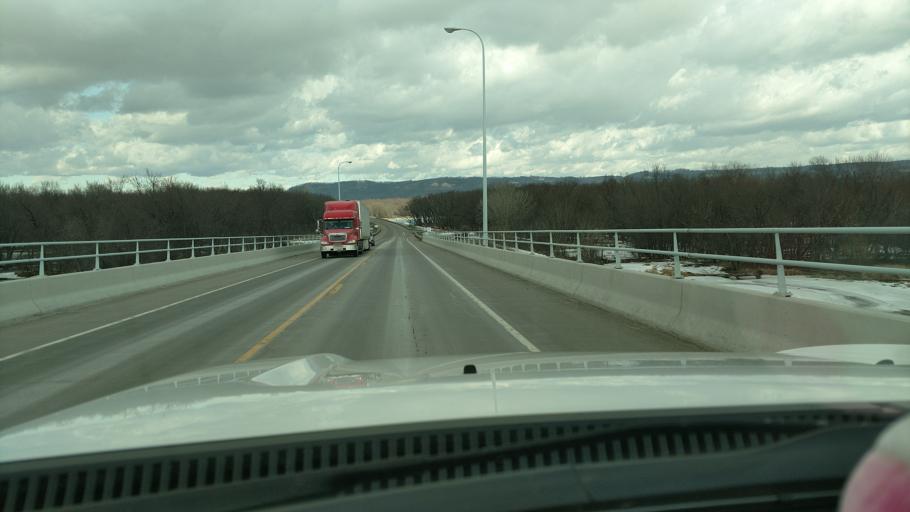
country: US
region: Minnesota
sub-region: Wabasha County
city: Wabasha
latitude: 44.3882
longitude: -92.0308
